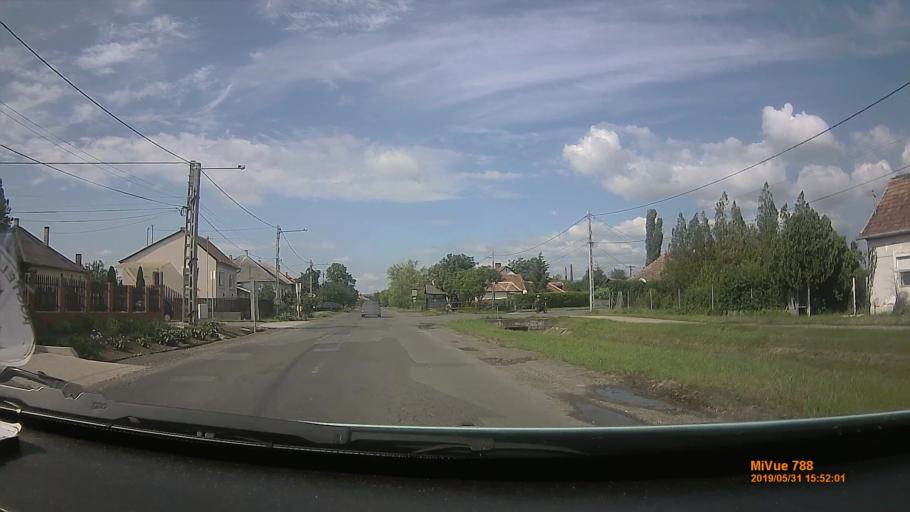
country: HU
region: Borsod-Abauj-Zemplen
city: Szerencs
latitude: 48.1482
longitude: 21.2009
